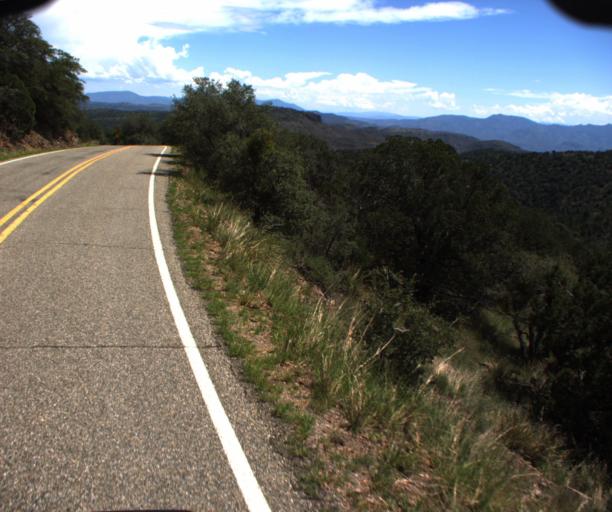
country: US
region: Arizona
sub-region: Greenlee County
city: Morenci
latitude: 33.2554
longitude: -109.3699
